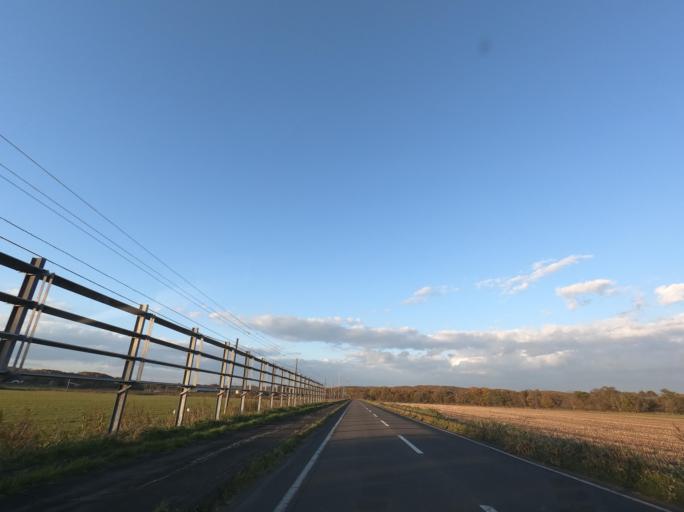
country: JP
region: Hokkaido
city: Kushiro
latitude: 43.2121
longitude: 144.4296
